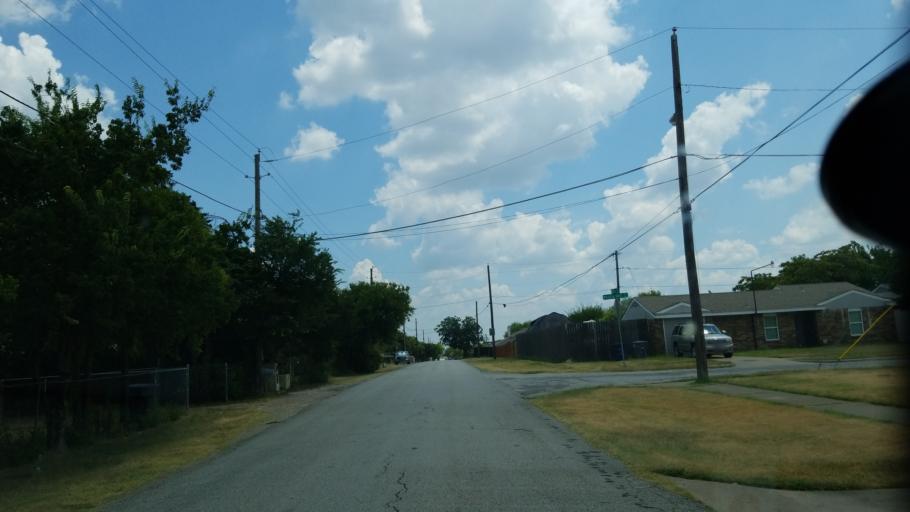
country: US
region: Texas
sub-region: Dallas County
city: Duncanville
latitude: 32.6814
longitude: -96.9006
